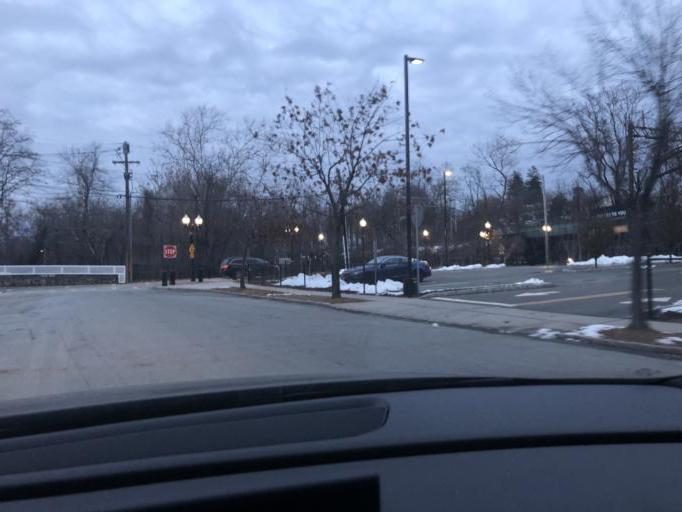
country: US
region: New Jersey
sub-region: Morris County
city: Morristown
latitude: 40.8008
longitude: -74.4773
